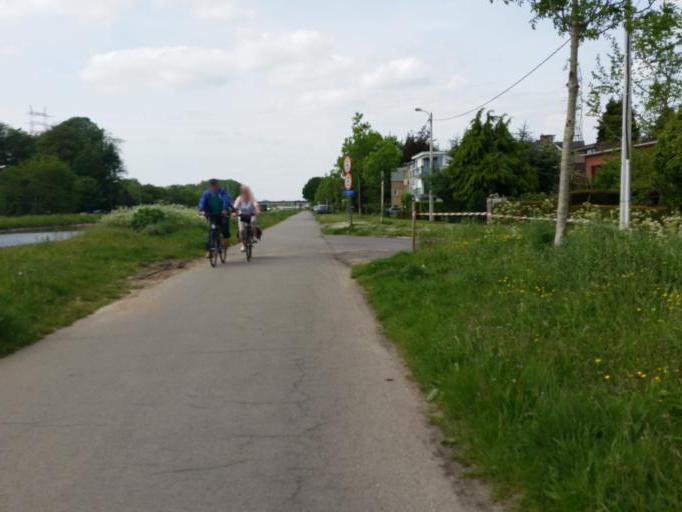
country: BE
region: Flanders
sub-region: Provincie Antwerpen
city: Mechelen
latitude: 51.0318
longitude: 4.4566
